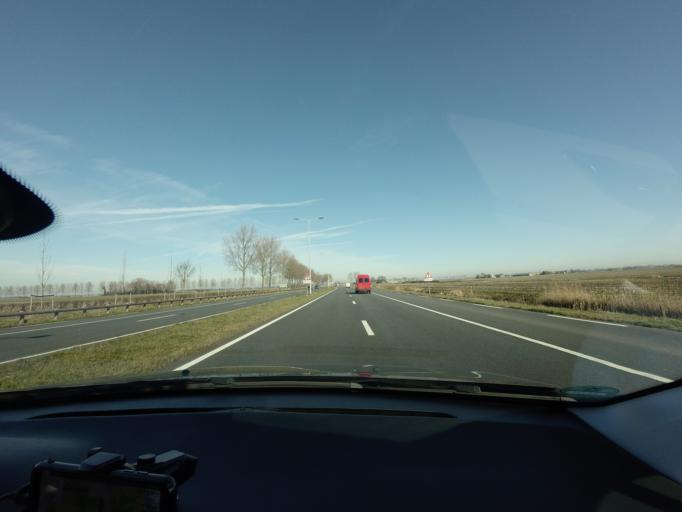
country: NL
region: South Holland
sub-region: Gemeente Alphen aan den Rijn
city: Alphen aan den Rijn
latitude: 52.1633
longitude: 4.6668
